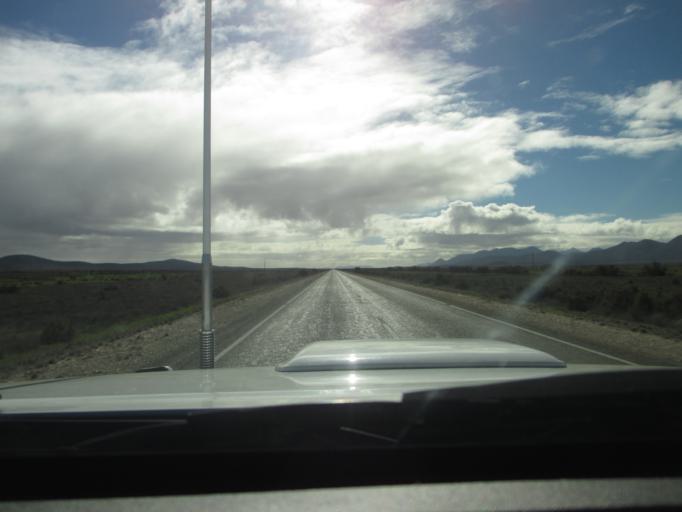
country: AU
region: South Australia
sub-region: Flinders Ranges
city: Quorn
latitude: -31.6825
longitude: 138.3652
